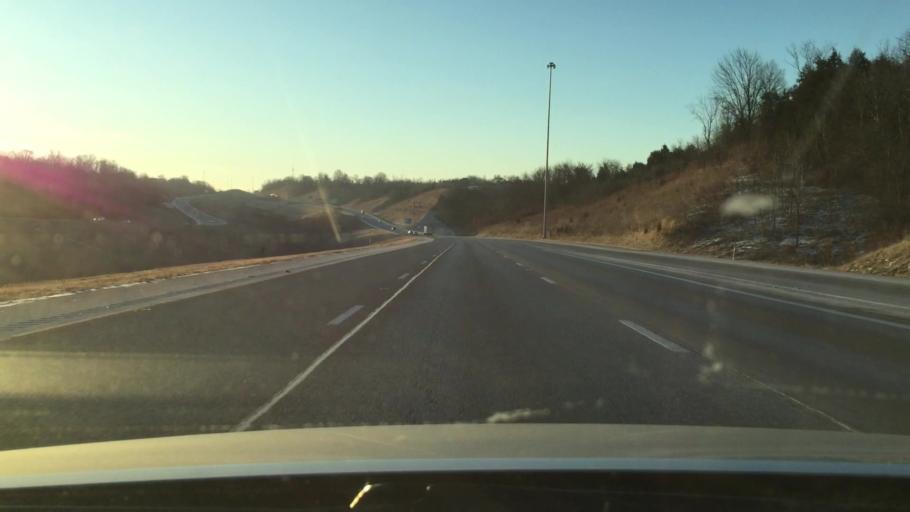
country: US
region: Kentucky
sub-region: Grant County
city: Williamstown
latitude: 38.6424
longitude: -84.5857
